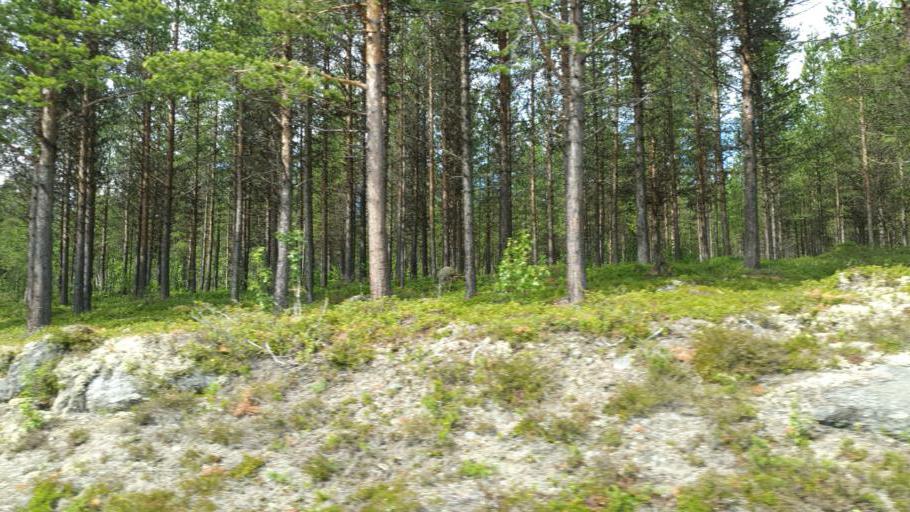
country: NO
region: Oppland
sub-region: Vaga
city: Vagamo
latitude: 61.6911
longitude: 9.0583
